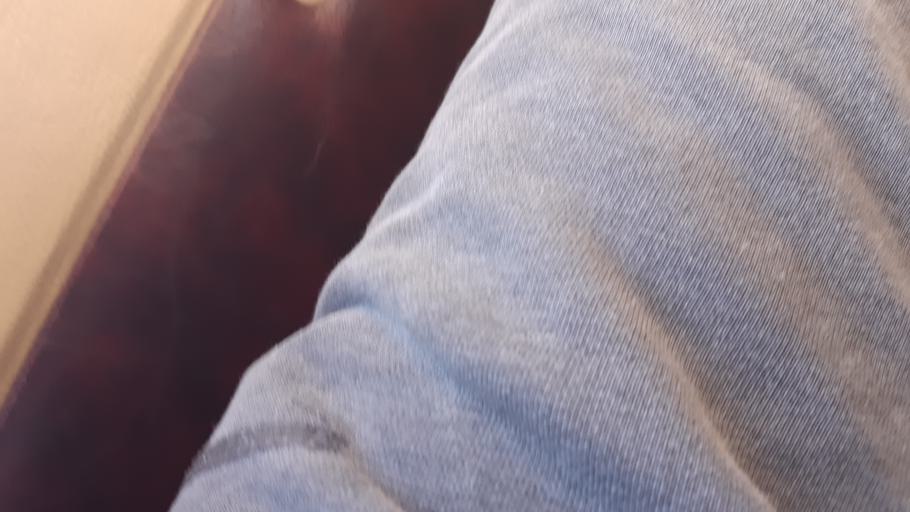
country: TR
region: Izmir
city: Urla
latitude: 38.3239
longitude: 26.7269
